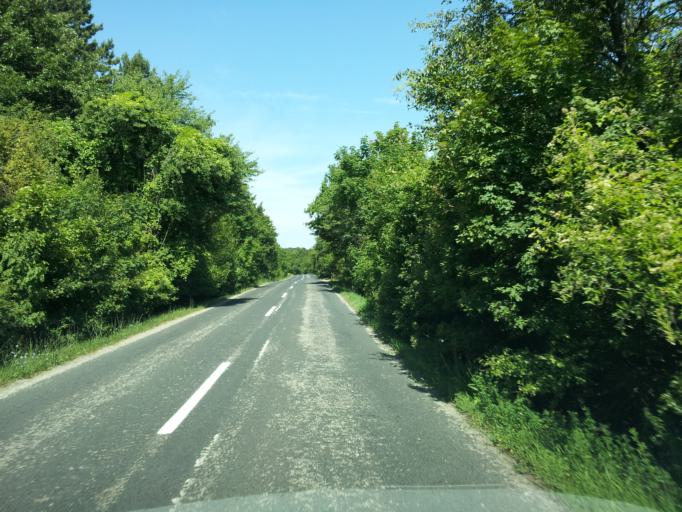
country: HU
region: Fejer
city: Szarliget
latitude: 47.5092
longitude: 18.5486
